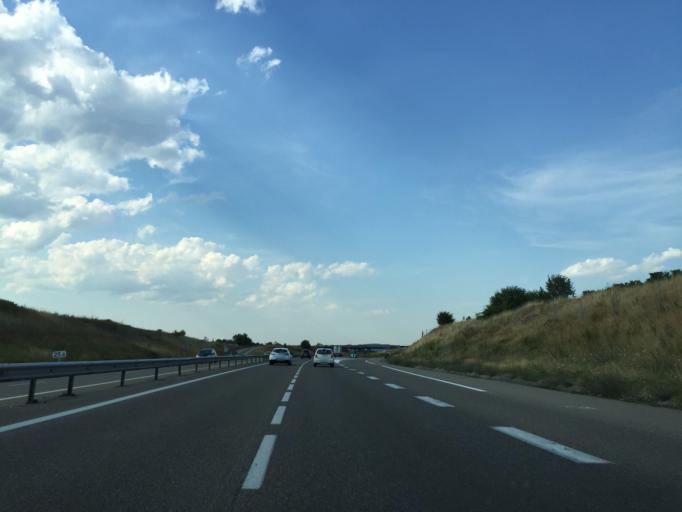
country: FR
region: Alsace
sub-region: Departement du Bas-Rhin
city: Stotzheim
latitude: 48.3922
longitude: 7.4762
